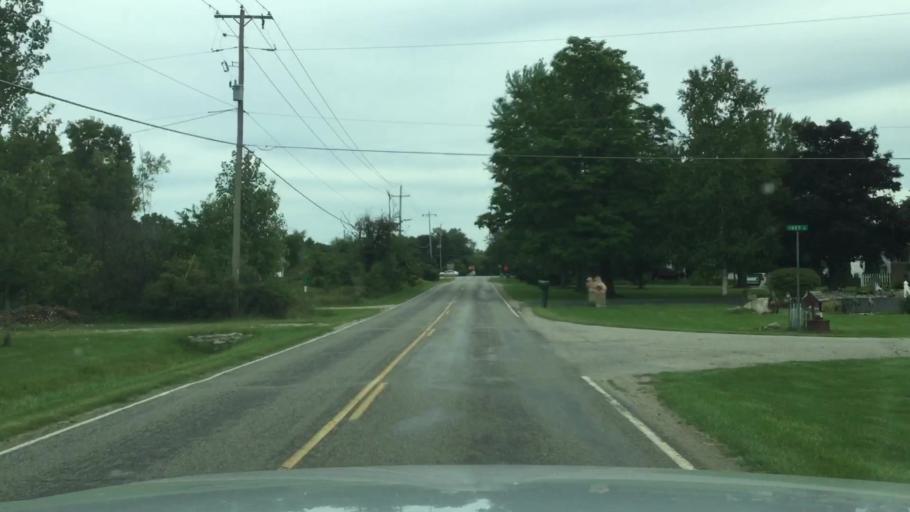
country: US
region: Michigan
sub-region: Shiawassee County
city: Durand
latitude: 42.9517
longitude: -83.9324
